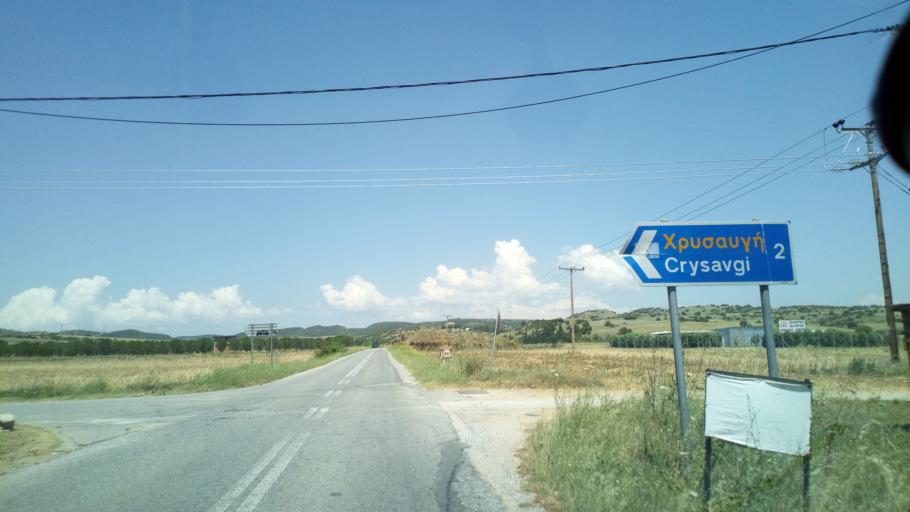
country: GR
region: Central Macedonia
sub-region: Nomos Thessalonikis
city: Lagkadas
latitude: 40.7699
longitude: 23.0985
